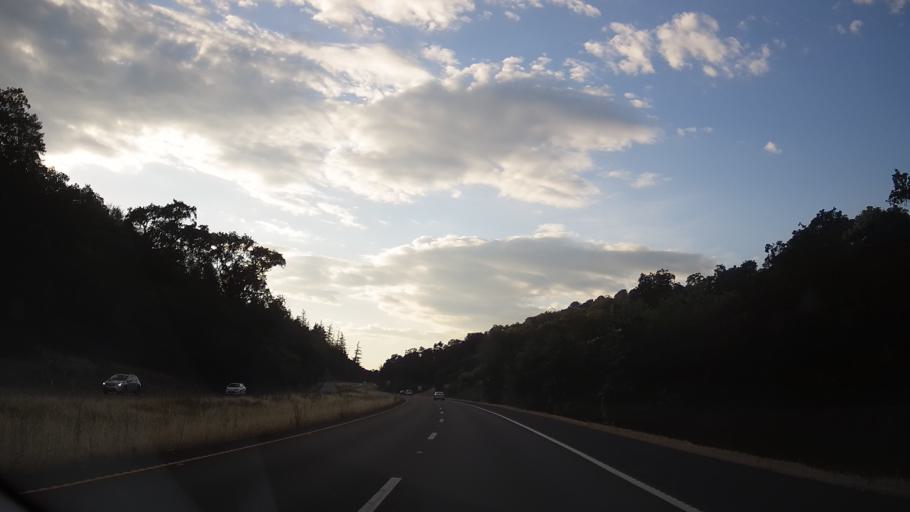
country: US
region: California
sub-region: Mendocino County
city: Talmage
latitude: 39.0619
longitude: -123.1622
